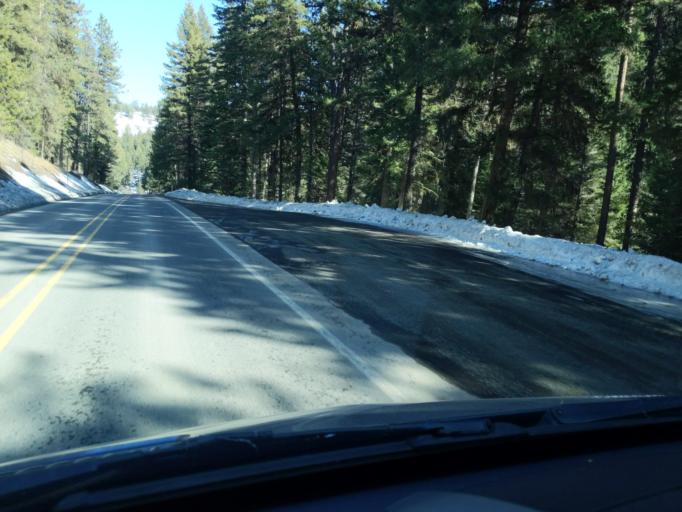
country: US
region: Oregon
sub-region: Grant County
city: John Day
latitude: 44.9403
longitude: -119.0047
